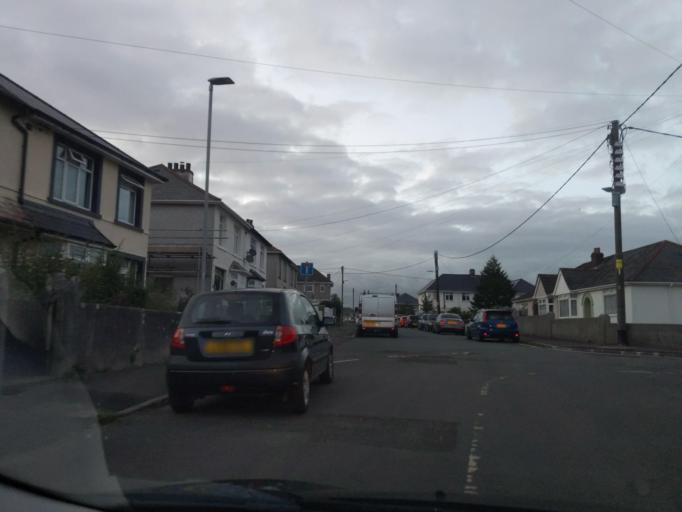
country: GB
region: England
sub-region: Plymouth
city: Plymstock
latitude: 50.3593
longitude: -4.0995
